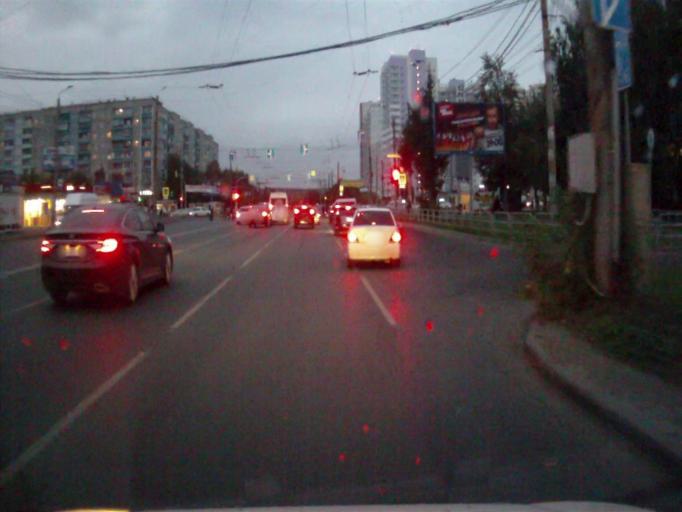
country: RU
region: Chelyabinsk
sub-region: Gorod Chelyabinsk
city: Chelyabinsk
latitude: 55.1797
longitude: 61.3326
